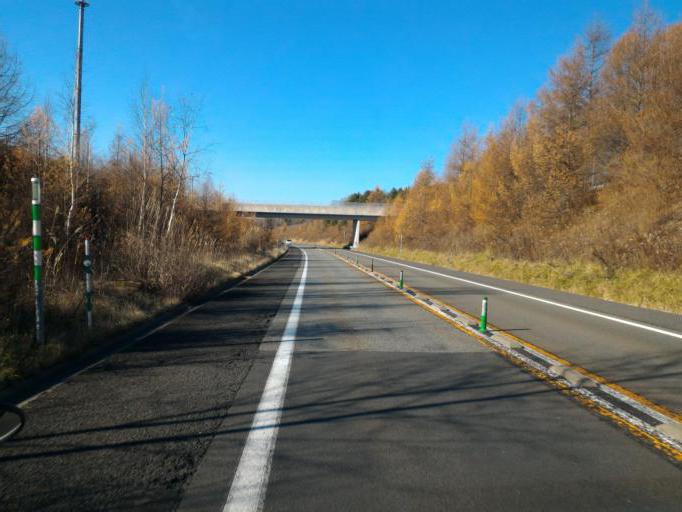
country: JP
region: Hokkaido
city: Chitose
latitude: 42.8976
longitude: 141.8551
